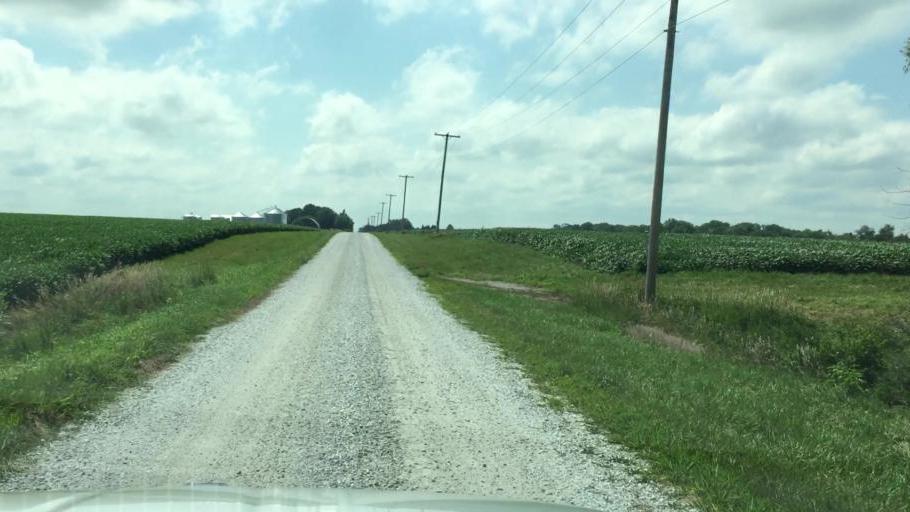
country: US
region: Illinois
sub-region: Hancock County
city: Carthage
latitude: 40.5357
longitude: -91.1587
